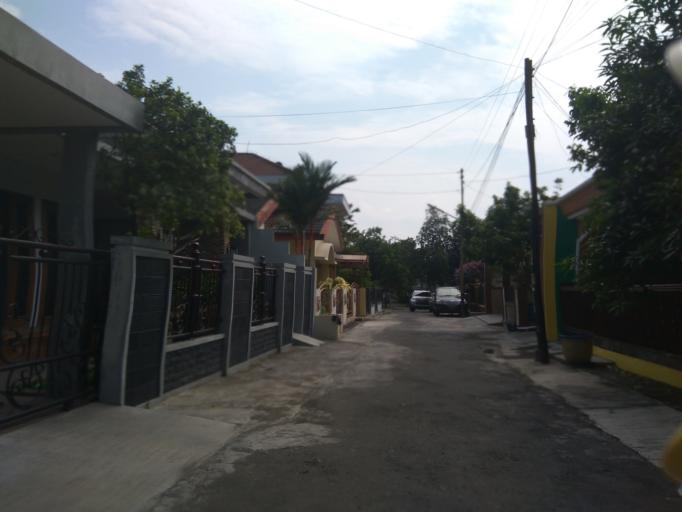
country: ID
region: Central Java
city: Semarang
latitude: -7.0451
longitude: 110.4174
